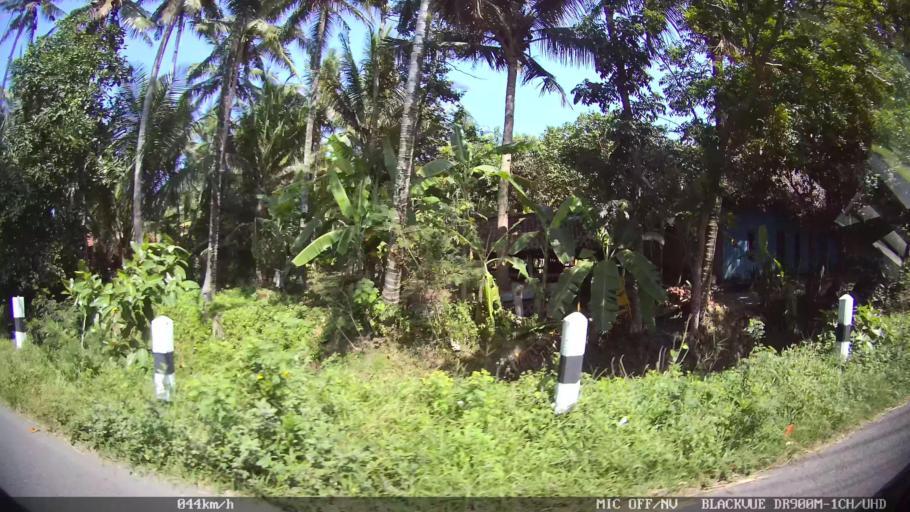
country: ID
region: Daerah Istimewa Yogyakarta
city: Srandakan
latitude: -7.9139
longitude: 110.1539
